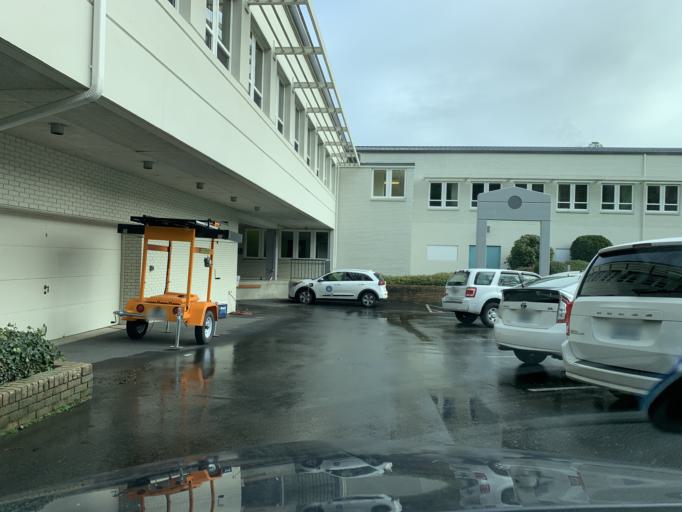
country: US
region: Washington
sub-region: King County
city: Mercer Island
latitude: 47.5775
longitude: -122.2110
